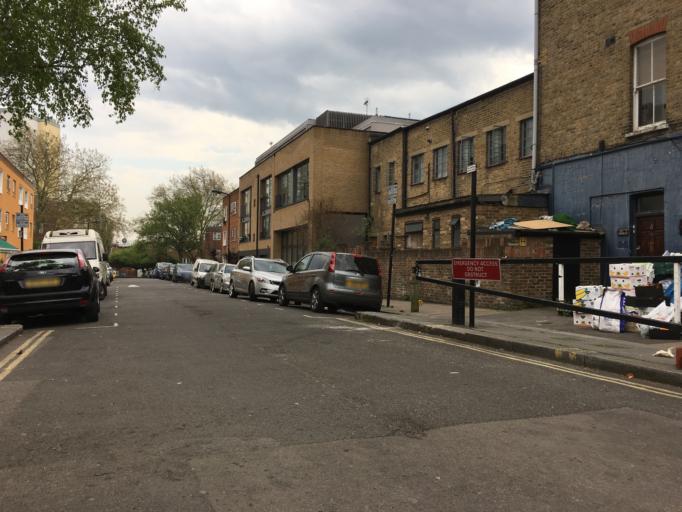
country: GB
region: England
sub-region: Greater London
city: Camden Town
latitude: 51.5503
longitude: -0.1509
